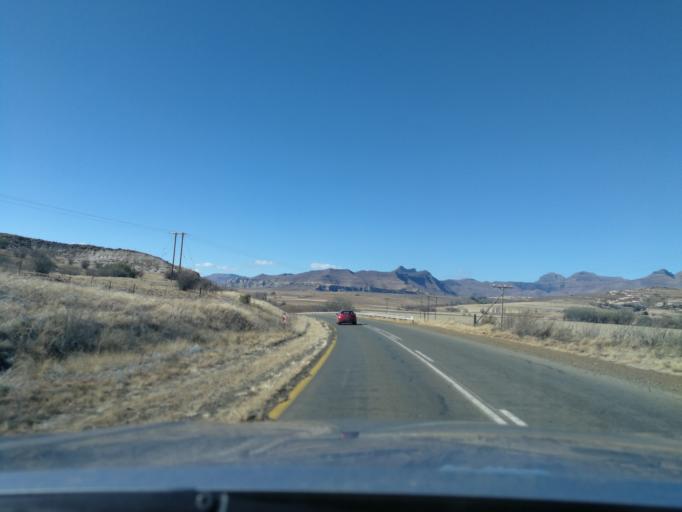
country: LS
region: Butha-Buthe
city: Butha-Buthe
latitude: -28.5299
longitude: 28.4704
